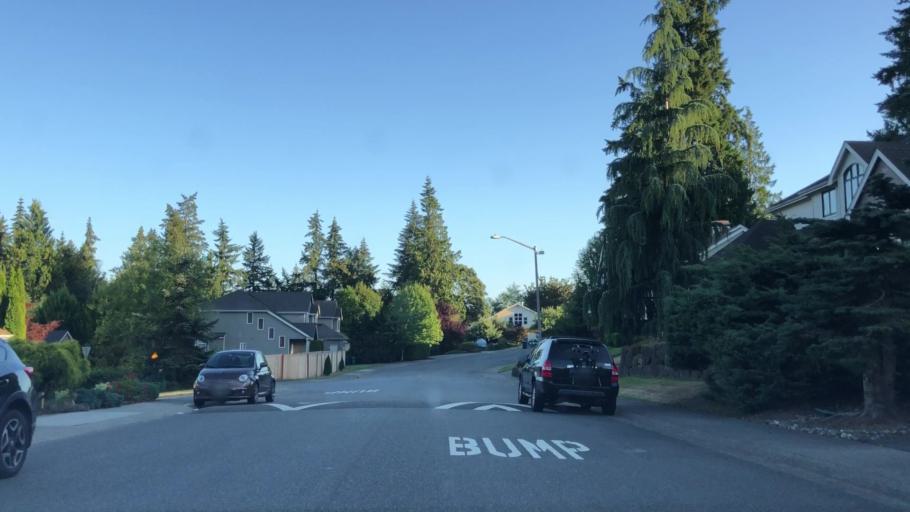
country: US
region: Washington
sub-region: King County
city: Redmond
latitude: 47.6906
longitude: -122.0958
